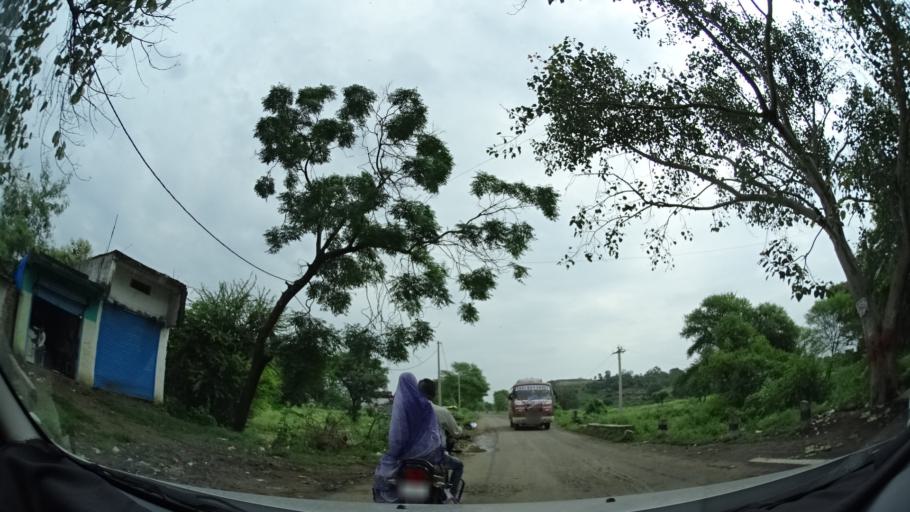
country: IN
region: Madhya Pradesh
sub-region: Raisen
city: Sultanpur
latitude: 23.3041
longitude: 78.0047
